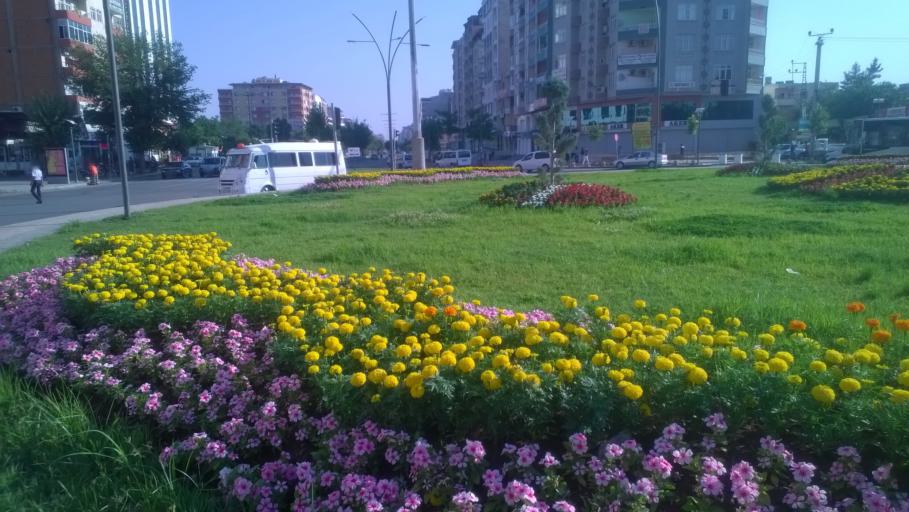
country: TR
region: Batman
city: Batman
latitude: 37.8894
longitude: 41.1292
